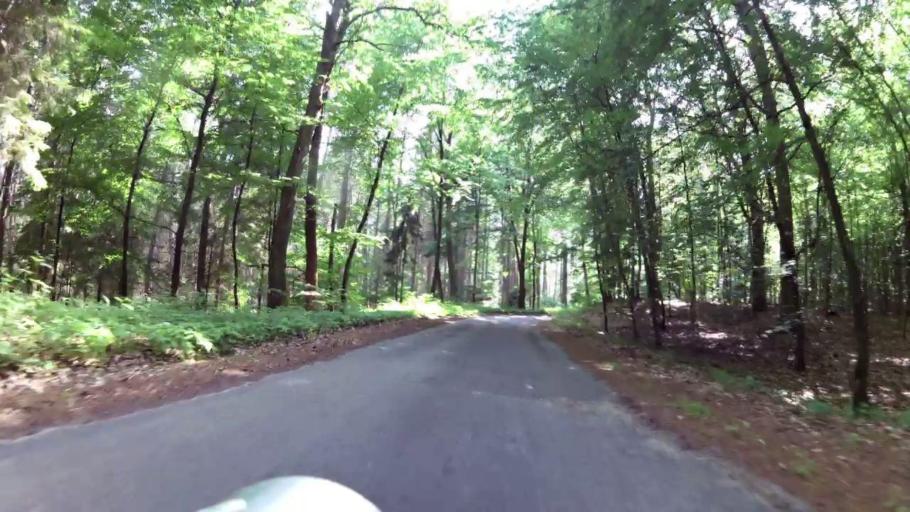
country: PL
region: West Pomeranian Voivodeship
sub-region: Powiat koszalinski
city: Bobolice
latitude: 53.9450
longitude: 16.6731
